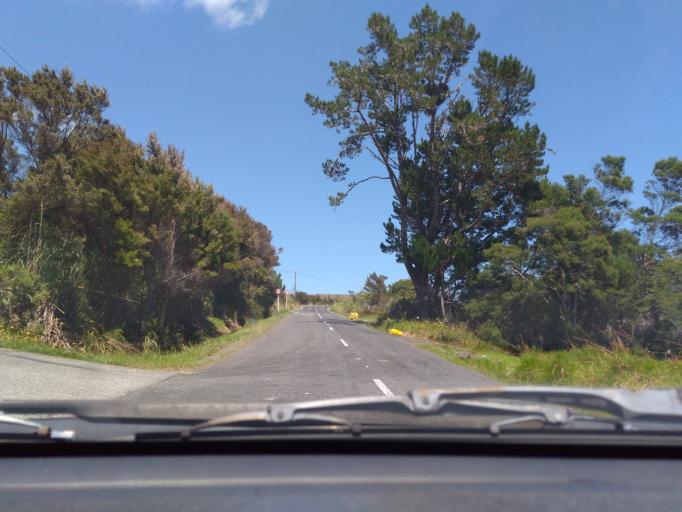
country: NZ
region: Northland
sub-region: Far North District
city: Taipa
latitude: -34.9941
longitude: 173.5267
